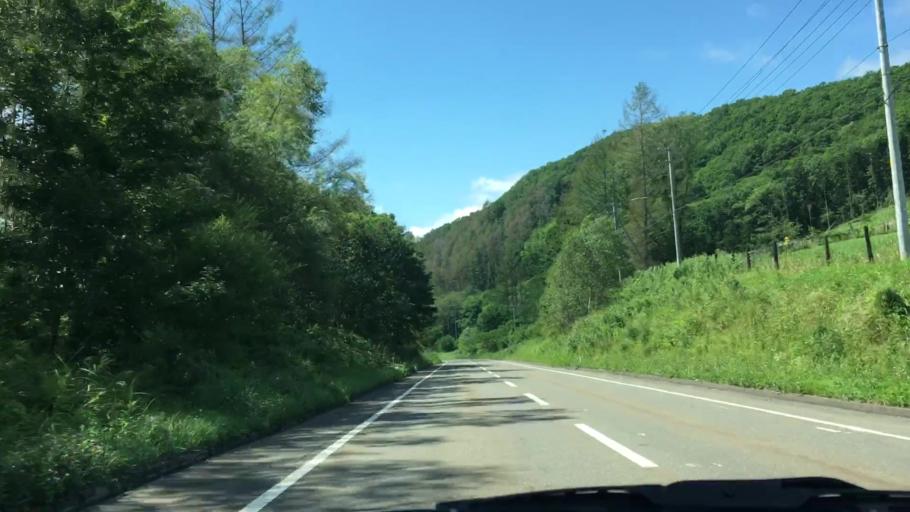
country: JP
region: Hokkaido
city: Kitami
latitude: 43.2937
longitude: 143.6686
